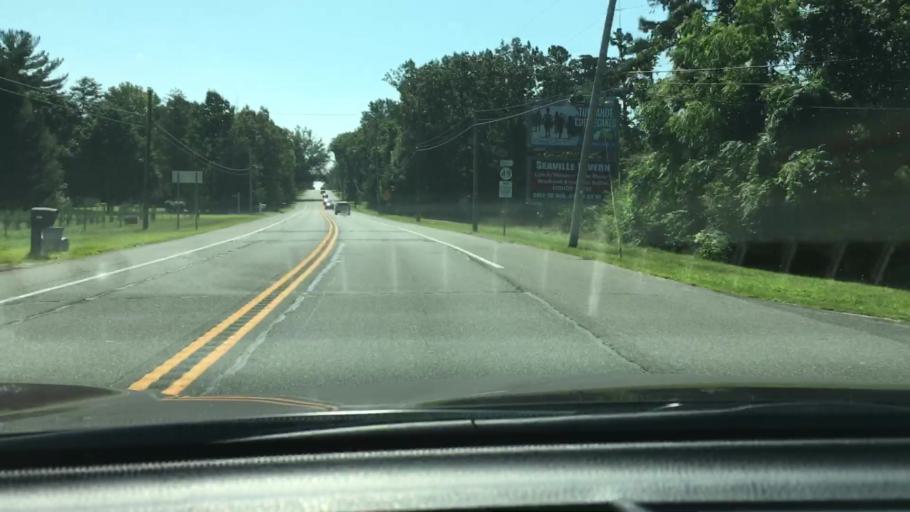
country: US
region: New Jersey
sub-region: Cumberland County
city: Laurel Lake
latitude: 39.3700
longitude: -74.9416
